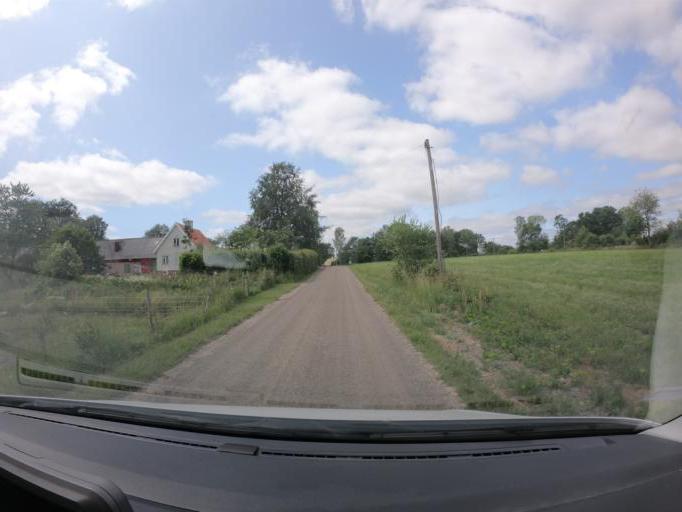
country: SE
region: Skane
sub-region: Hassleholms Kommun
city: Sosdala
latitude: 55.9838
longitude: 13.6442
